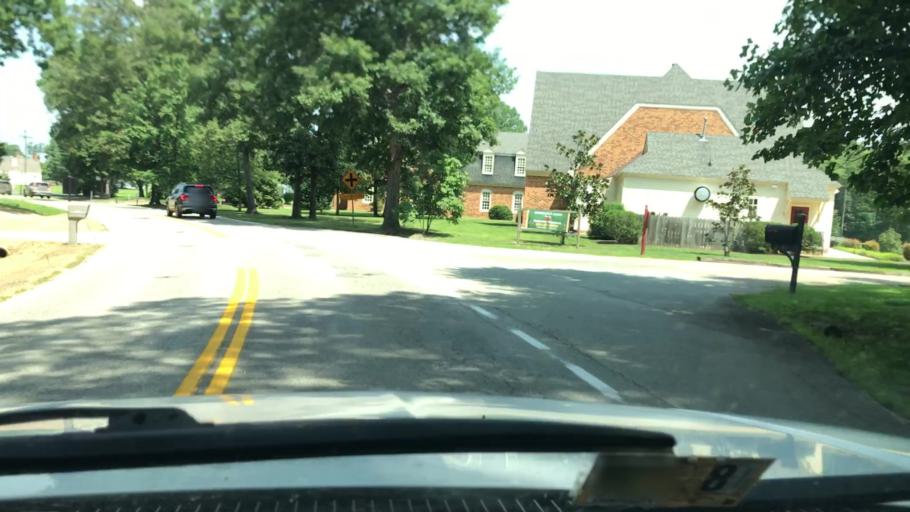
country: US
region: Virginia
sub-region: Chesterfield County
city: Brandermill
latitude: 37.5228
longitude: -77.6642
